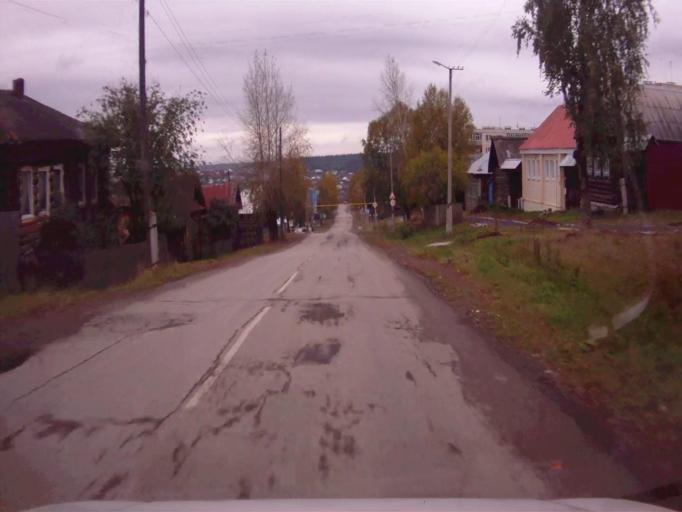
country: RU
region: Chelyabinsk
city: Nyazepetrovsk
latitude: 56.0572
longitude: 59.6077
